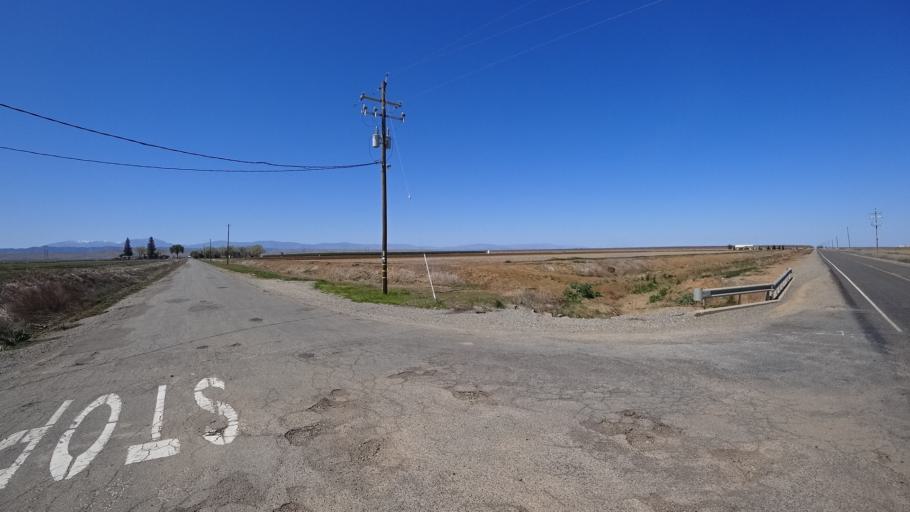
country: US
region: California
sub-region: Glenn County
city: Willows
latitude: 39.4655
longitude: -122.2490
